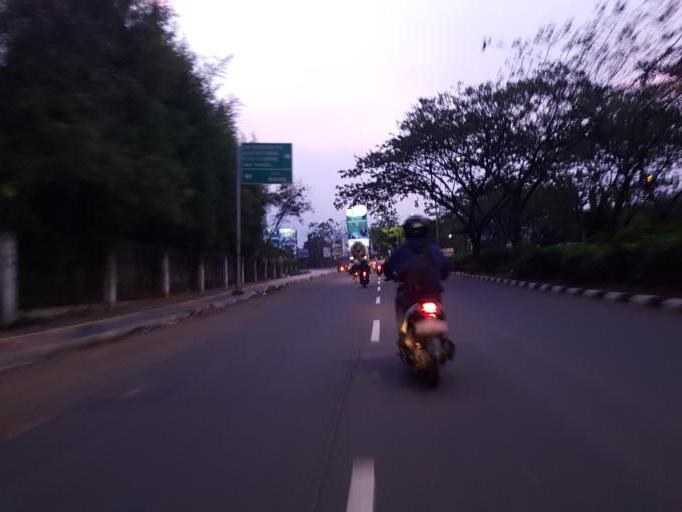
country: ID
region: West Java
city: Serpong
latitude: -6.3314
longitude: 106.6750
